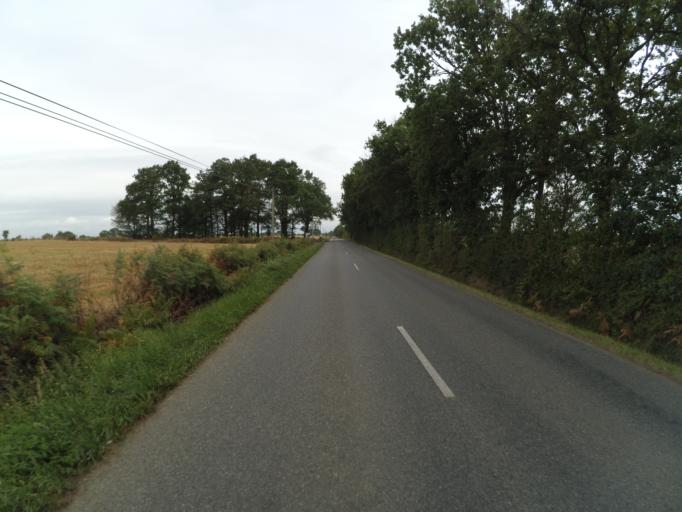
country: FR
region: Pays de la Loire
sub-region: Departement de la Vendee
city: Saint-Andre-Treize-Voies
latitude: 46.9544
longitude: -1.4191
